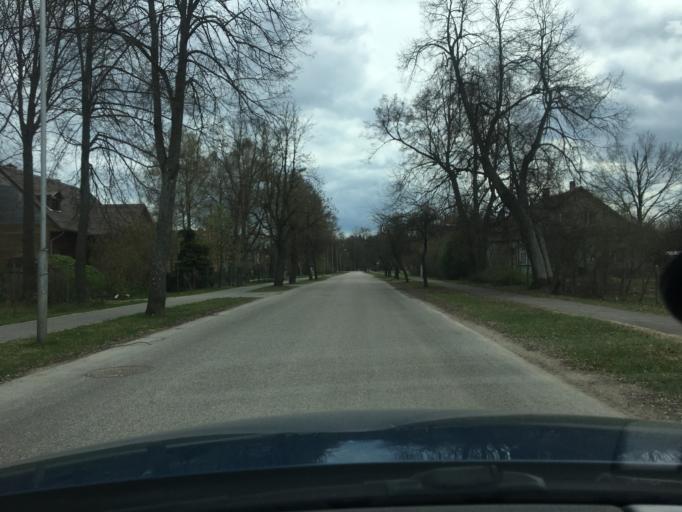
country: LV
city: Tireli
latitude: 56.9441
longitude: 23.4894
